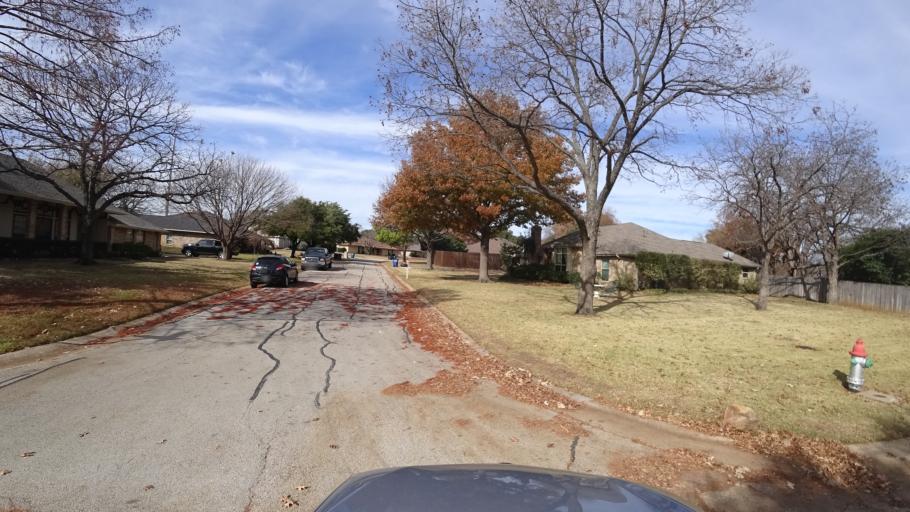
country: US
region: Texas
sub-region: Denton County
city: Highland Village
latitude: 33.0827
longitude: -97.0427
